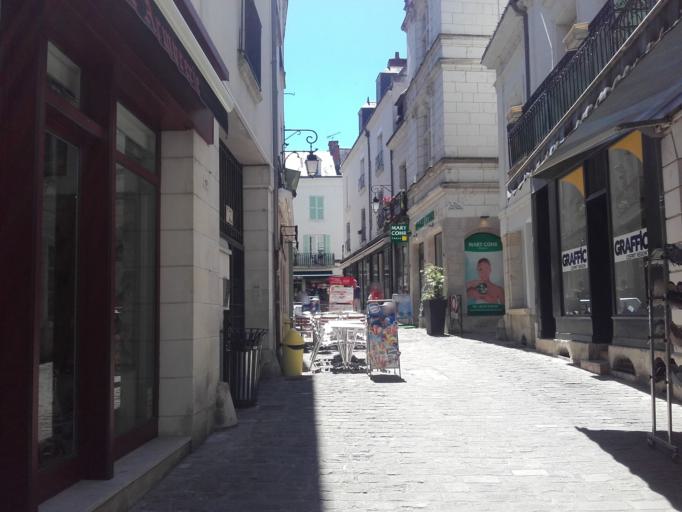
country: FR
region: Centre
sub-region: Departement d'Indre-et-Loire
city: Loches
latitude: 47.1283
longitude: 0.9984
